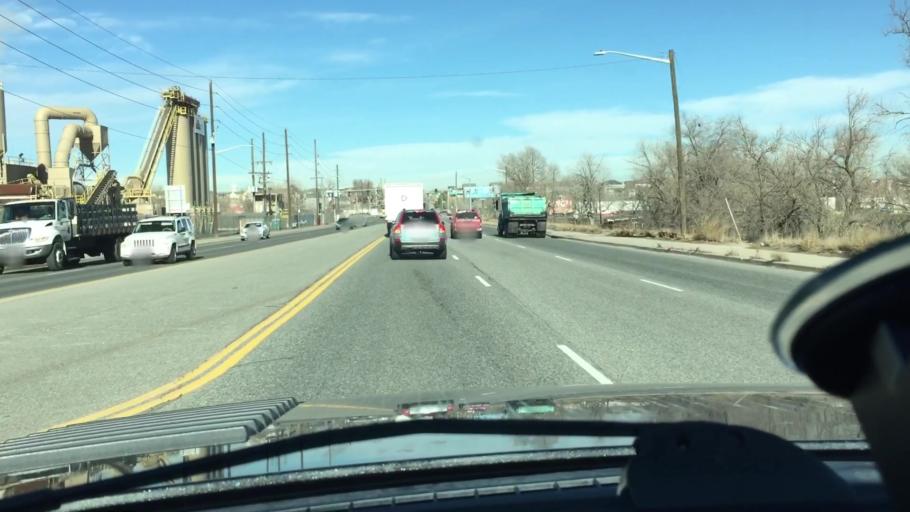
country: US
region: Colorado
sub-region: Adams County
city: Twin Lakes
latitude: 39.8112
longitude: -105.0062
